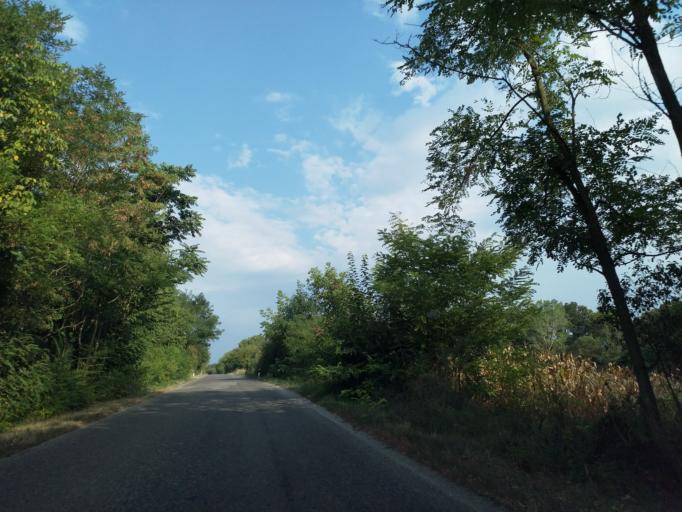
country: RS
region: Central Serbia
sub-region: Pomoravski Okrug
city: Paracin
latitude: 43.8486
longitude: 21.4557
